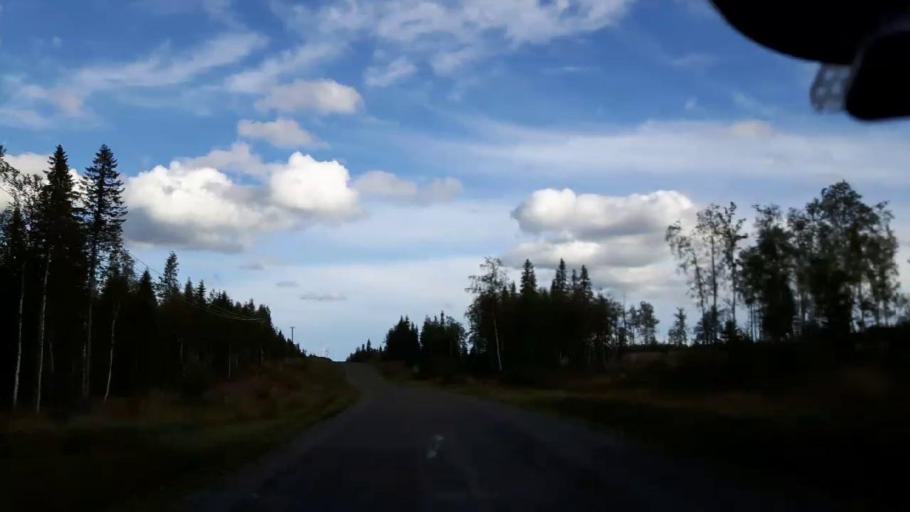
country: SE
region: Jaemtland
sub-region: Ragunda Kommun
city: Hammarstrand
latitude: 63.4396
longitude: 15.9916
